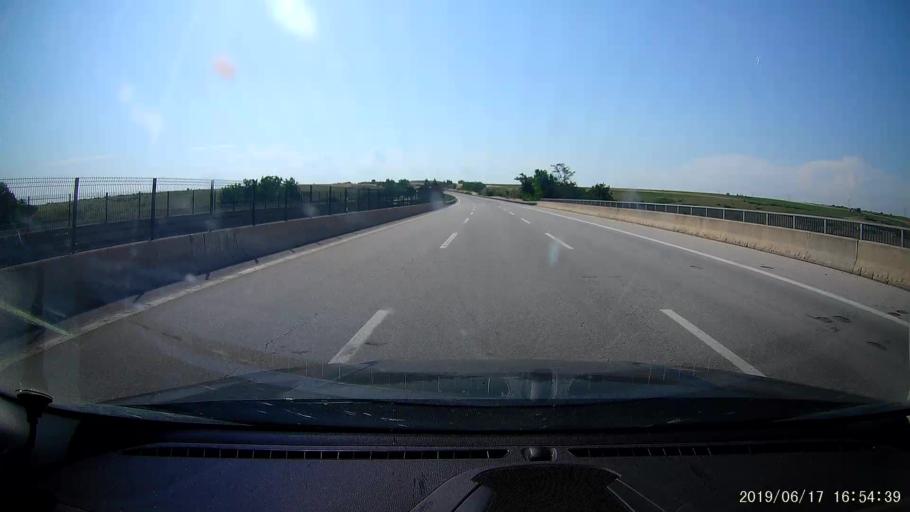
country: TR
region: Kirklareli
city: Inece
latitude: 41.5754
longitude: 26.9896
